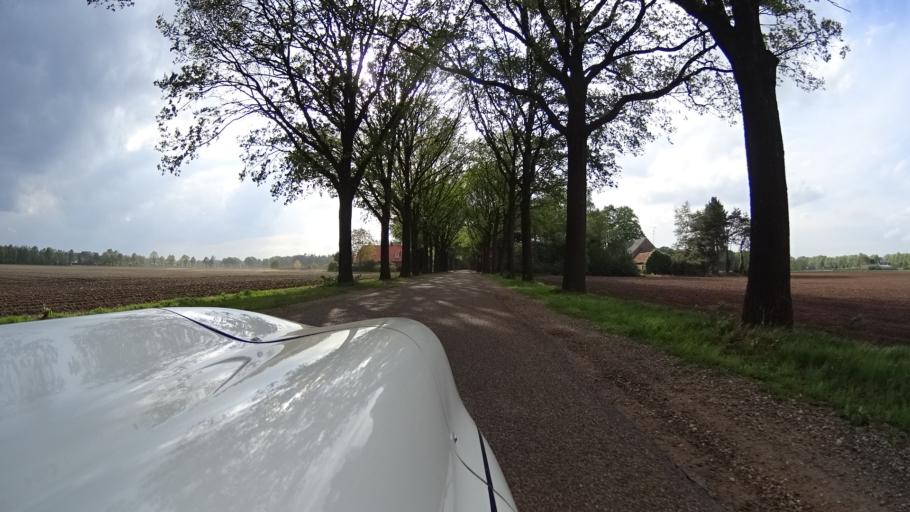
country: NL
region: North Brabant
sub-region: Gemeente Uden
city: Odiliapeel
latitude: 51.6362
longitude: 5.7173
